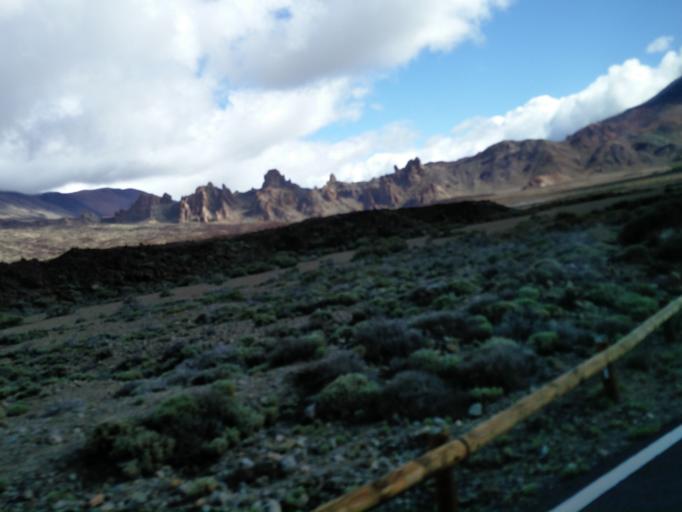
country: ES
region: Canary Islands
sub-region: Provincia de Santa Cruz de Tenerife
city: Vilaflor
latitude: 28.2110
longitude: -16.6538
